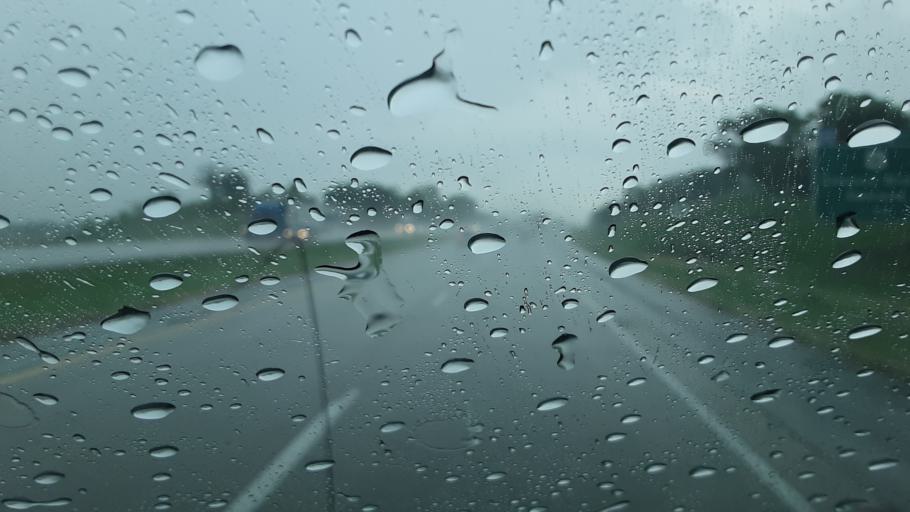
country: US
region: Iowa
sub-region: Pottawattamie County
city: Council Bluffs
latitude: 41.2654
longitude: -95.7990
